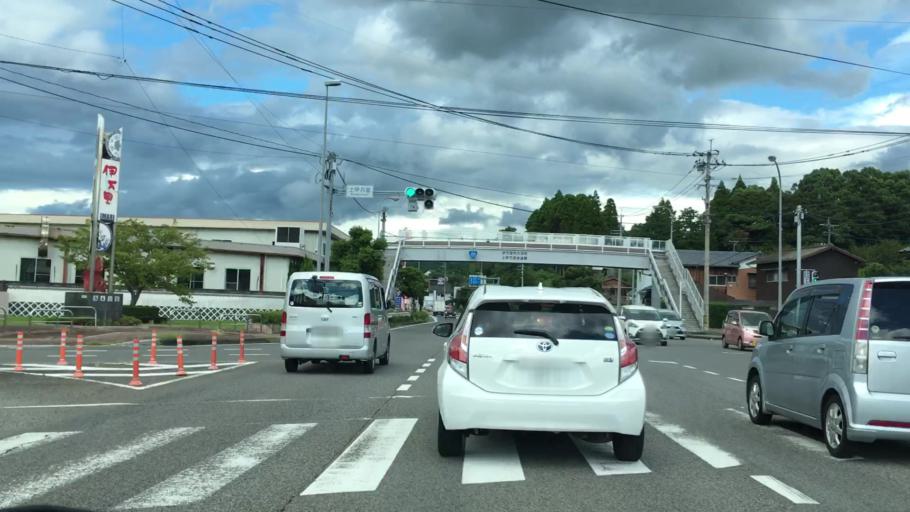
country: JP
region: Saga Prefecture
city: Imaricho-ko
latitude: 33.2729
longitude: 129.8903
